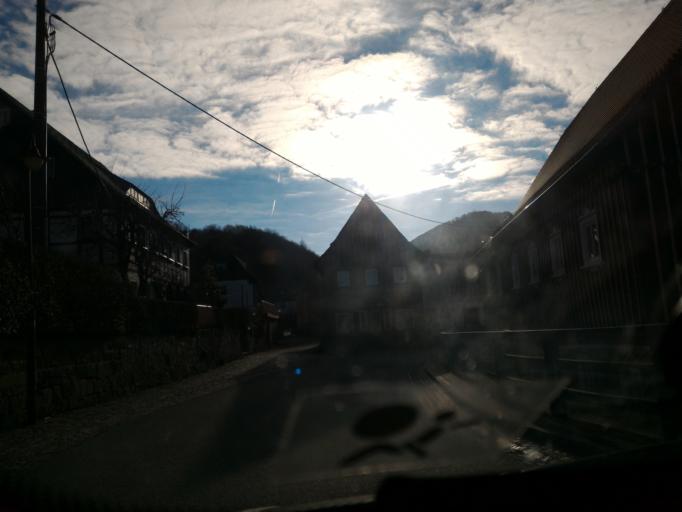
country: DE
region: Saxony
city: Grossschonau
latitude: 50.8685
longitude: 14.6495
